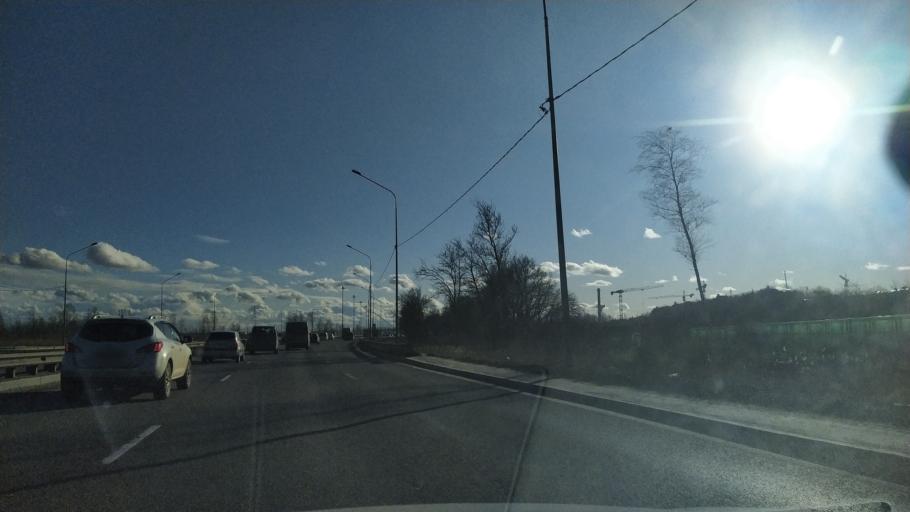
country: RU
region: St.-Petersburg
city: Aleksandrovskaya
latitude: 59.7639
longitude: 30.3294
